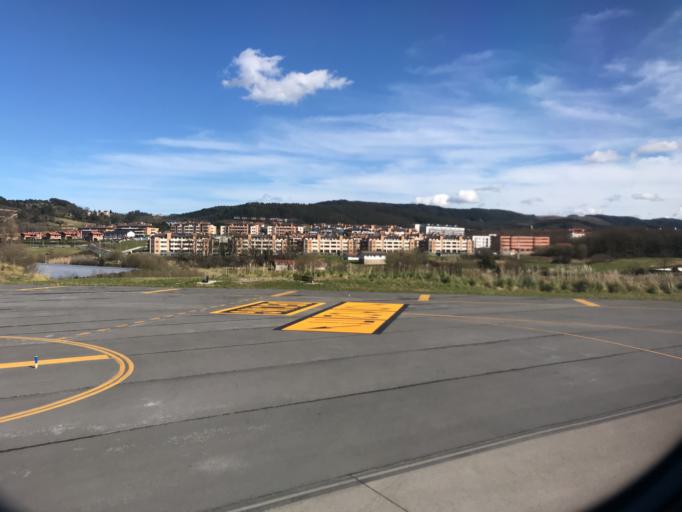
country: ES
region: Basque Country
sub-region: Bizkaia
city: Derio
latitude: 43.2977
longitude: -2.8962
